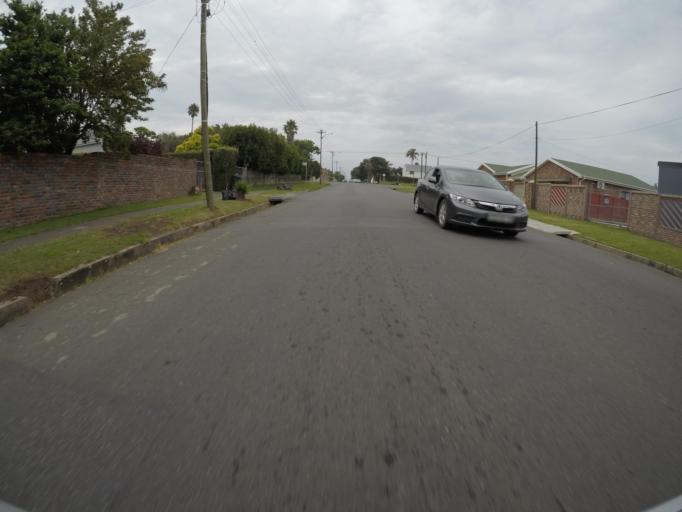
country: ZA
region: Eastern Cape
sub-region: Buffalo City Metropolitan Municipality
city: East London
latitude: -32.9778
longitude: 27.8944
